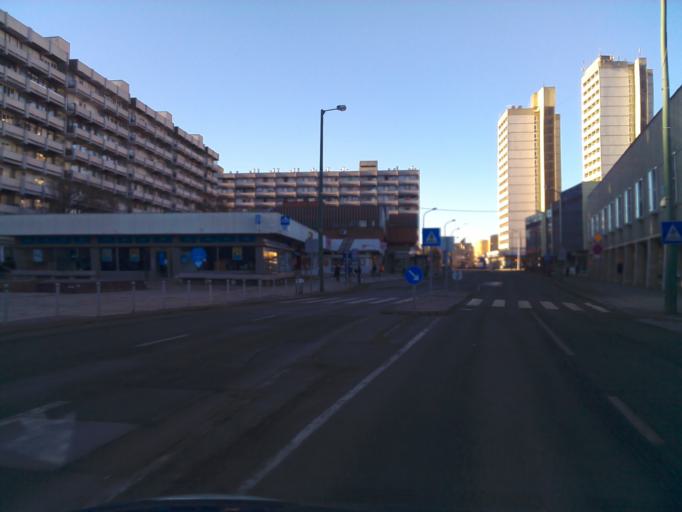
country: HU
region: Nograd
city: Salgotarjan
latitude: 48.1050
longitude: 19.8082
